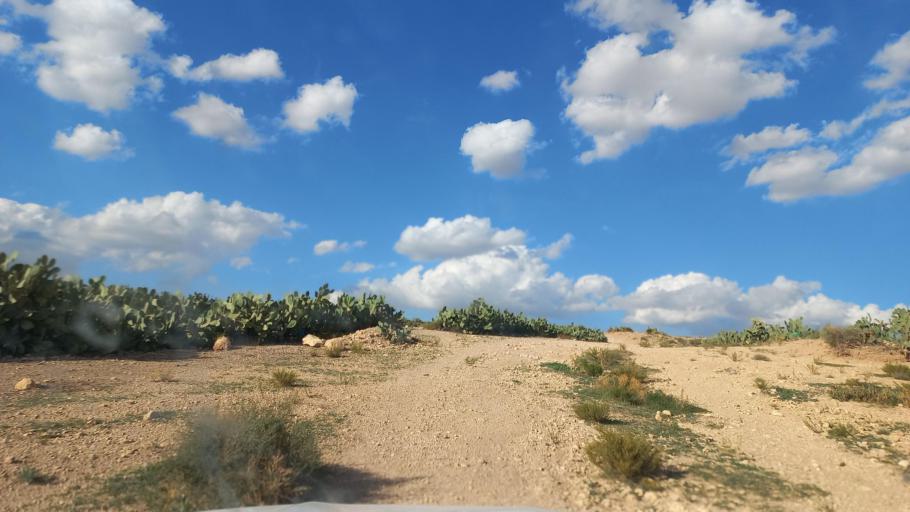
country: TN
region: Al Qasrayn
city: Sbiba
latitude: 35.3899
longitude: 9.0430
